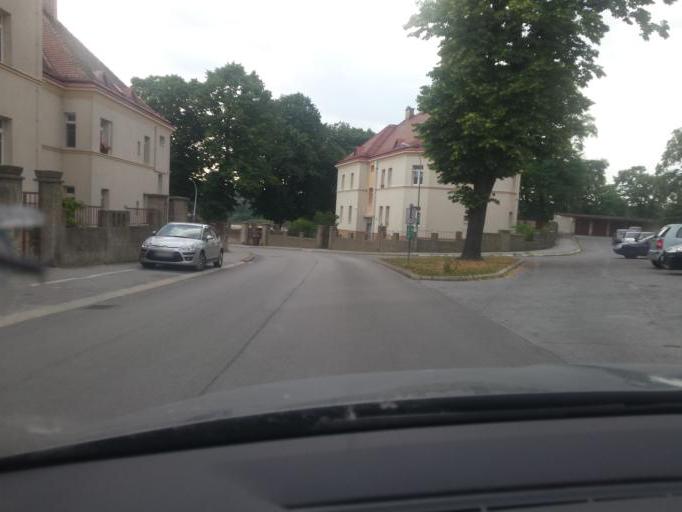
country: AT
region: Lower Austria
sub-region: Politischer Bezirk Bruck an der Leitha
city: Hainburg an der Donau
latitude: 48.1501
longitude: 16.9459
